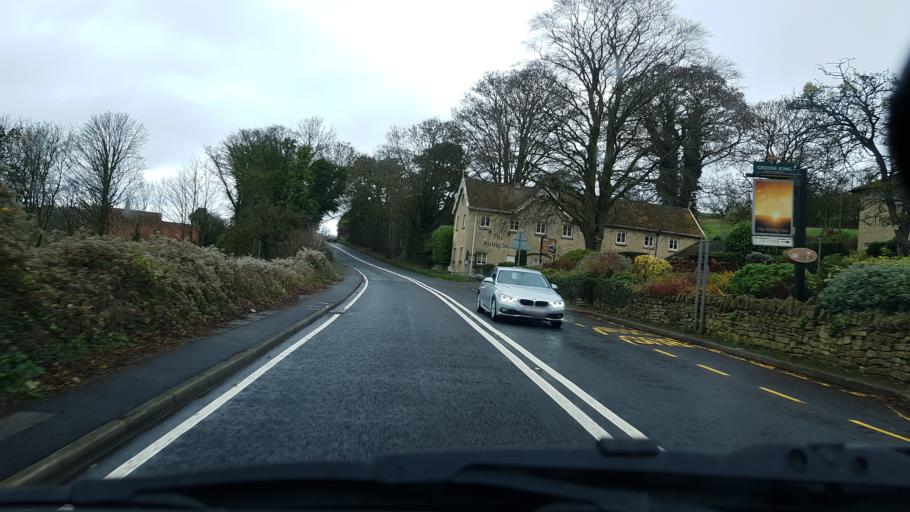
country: GB
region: England
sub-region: Gloucestershire
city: Gotherington
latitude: 51.9386
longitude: -2.0300
